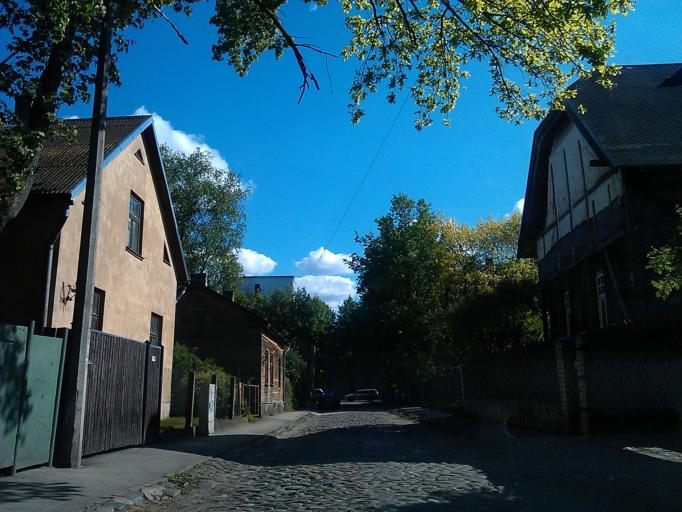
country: LV
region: Riga
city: Jaunciems
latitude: 56.9841
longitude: 24.1763
